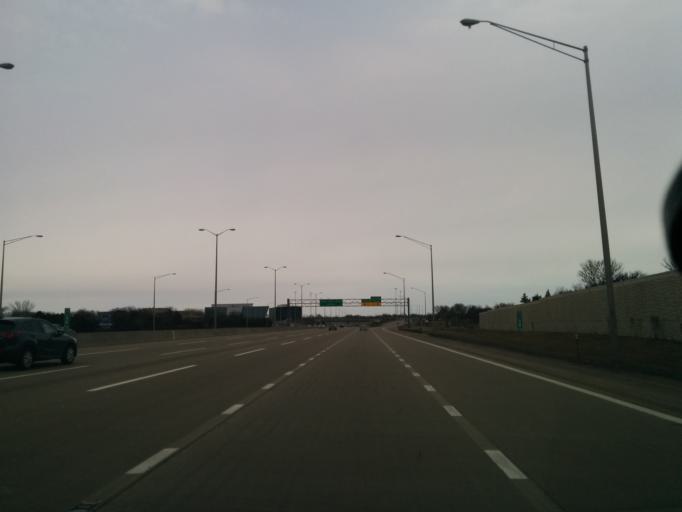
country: US
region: Illinois
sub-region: Cook County
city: Northbrook
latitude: 42.1003
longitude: -87.8679
